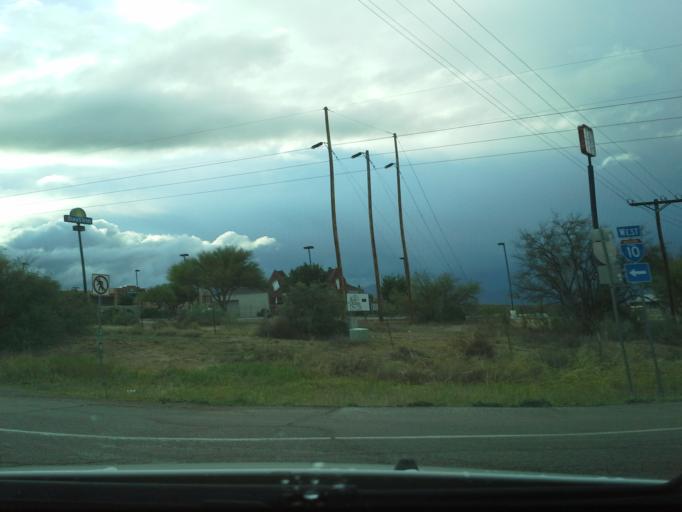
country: US
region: Arizona
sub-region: Cochise County
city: Benson
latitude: 31.9790
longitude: -110.3071
